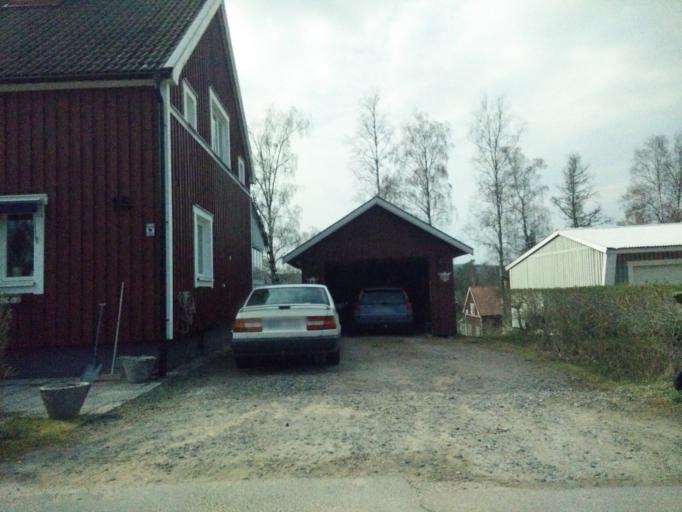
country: SE
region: Vaermland
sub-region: Munkfors Kommun
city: Munkfors
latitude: 59.8422
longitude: 13.5617
